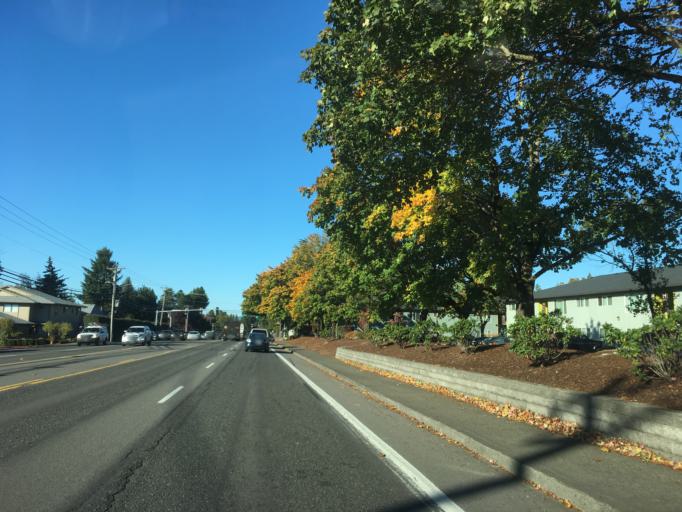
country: US
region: Oregon
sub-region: Multnomah County
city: Wood Village
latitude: 45.5082
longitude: -122.3999
